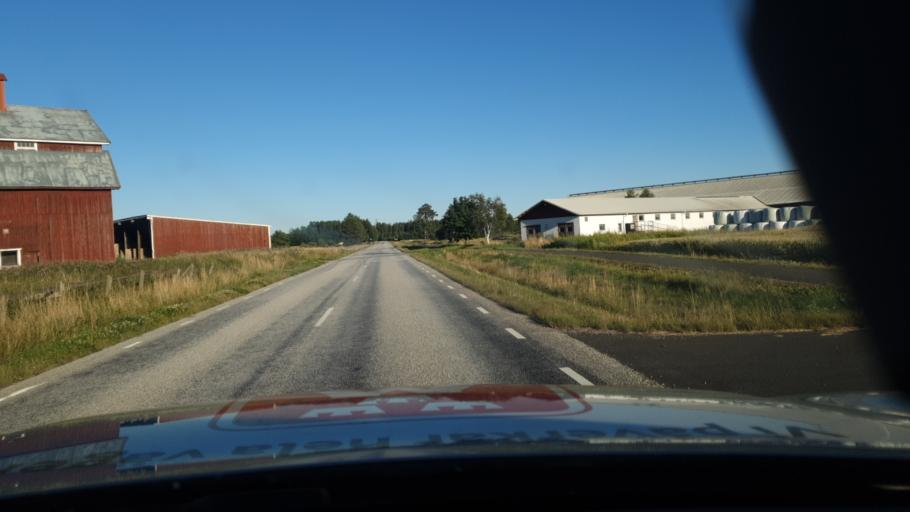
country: SE
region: Vaestra Goetaland
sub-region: Skovde Kommun
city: Stopen
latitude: 58.4783
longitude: 13.8929
